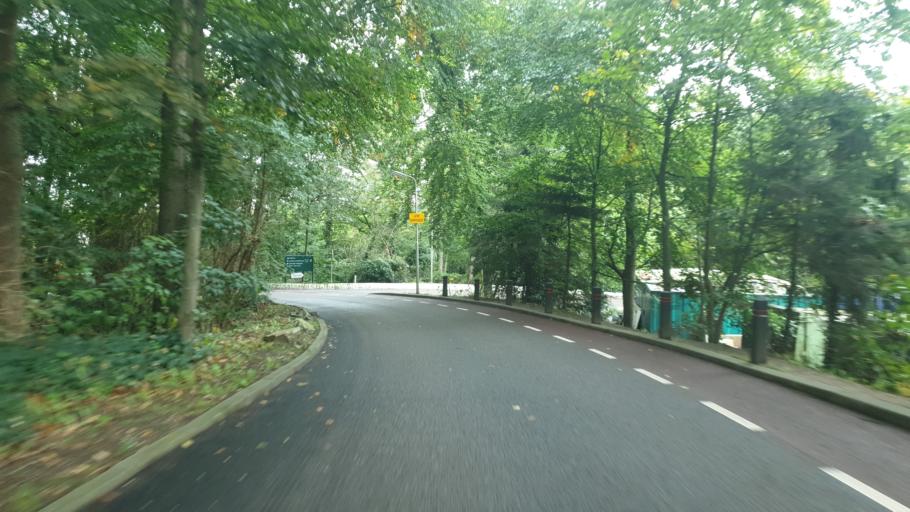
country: NL
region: Gelderland
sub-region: Gemeente Groesbeek
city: Berg en Dal
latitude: 51.8341
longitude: 5.8980
